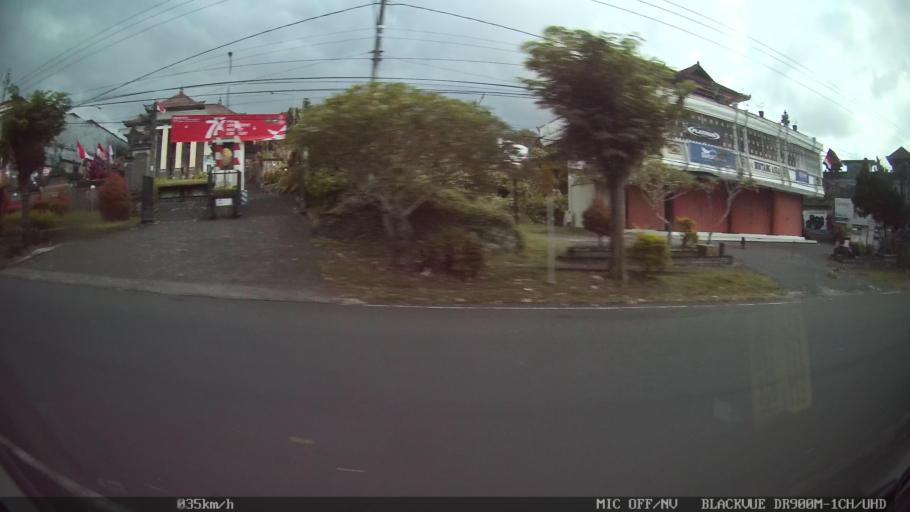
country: ID
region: Bali
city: Banjar Tegal Belodan
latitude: -8.5365
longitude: 115.1167
